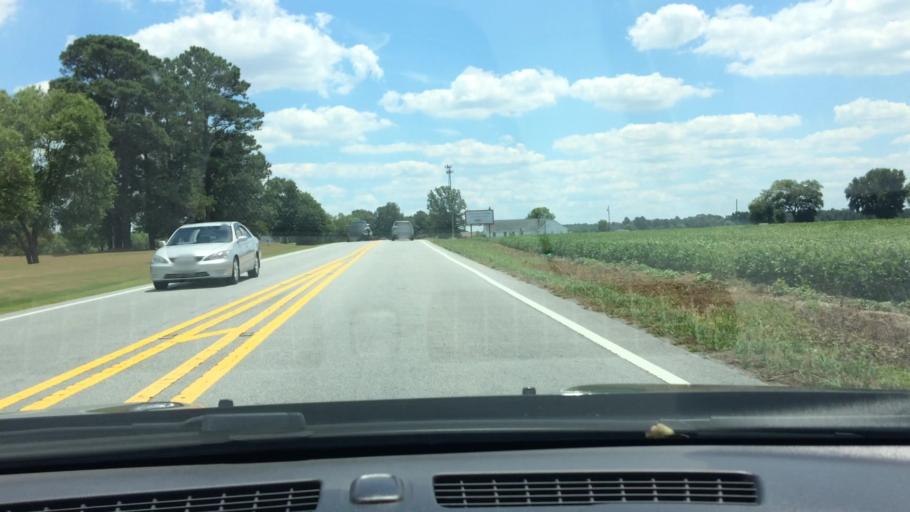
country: US
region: North Carolina
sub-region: Pitt County
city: Summerfield
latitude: 35.6381
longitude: -77.4516
